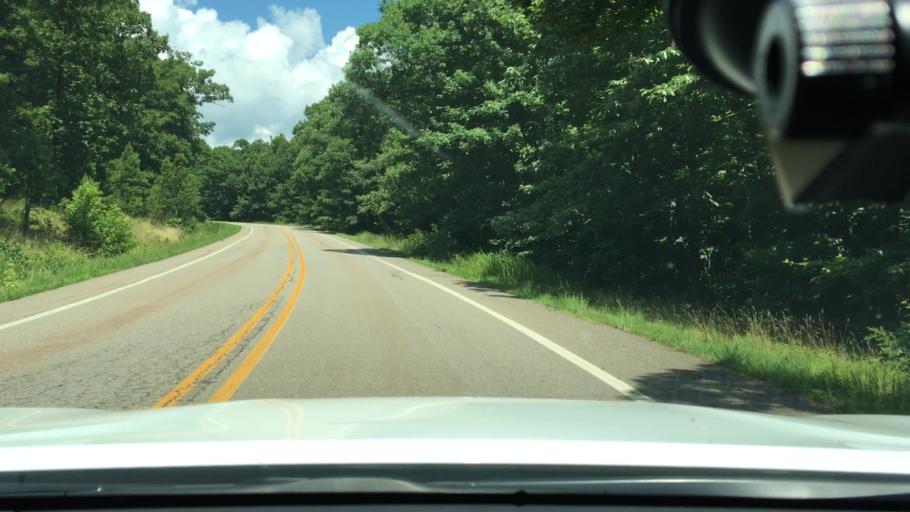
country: US
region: Arkansas
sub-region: Logan County
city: Paris
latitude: 35.1698
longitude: -93.6415
